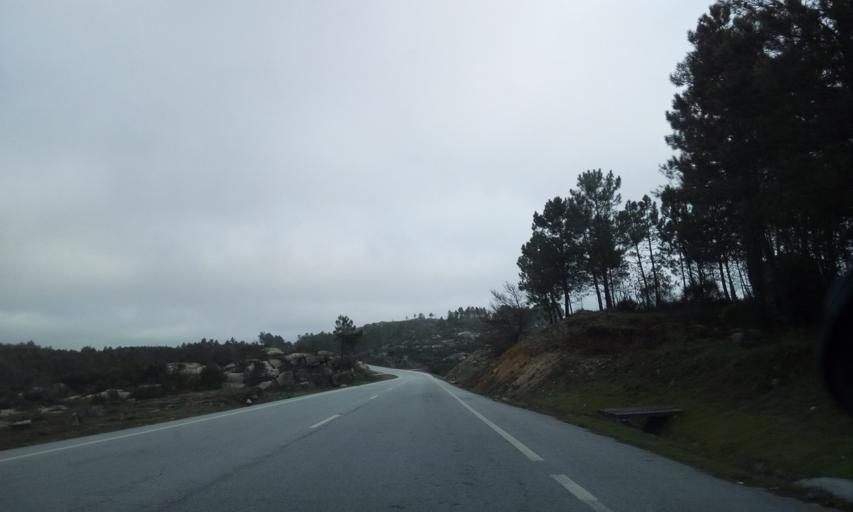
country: PT
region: Guarda
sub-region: Aguiar da Beira
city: Aguiar da Beira
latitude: 40.7556
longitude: -7.5036
